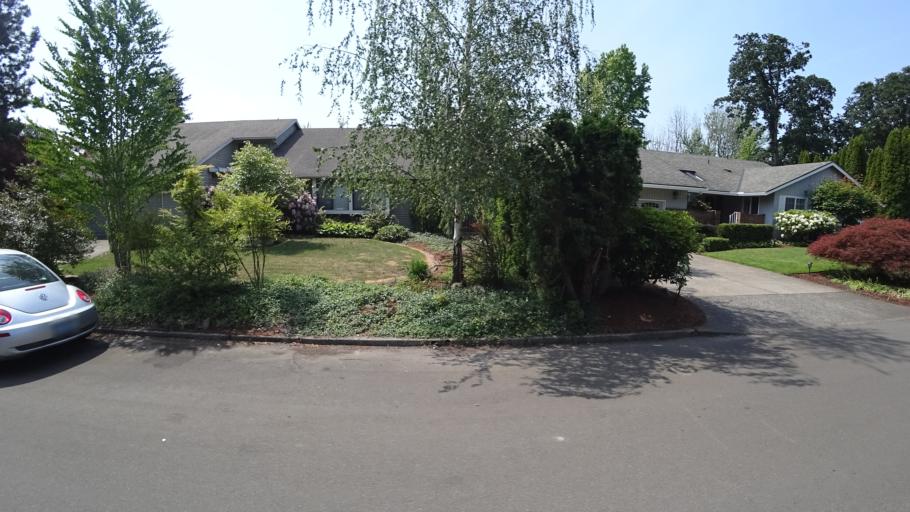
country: US
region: Oregon
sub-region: Washington County
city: Oak Hills
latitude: 45.5363
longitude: -122.8291
